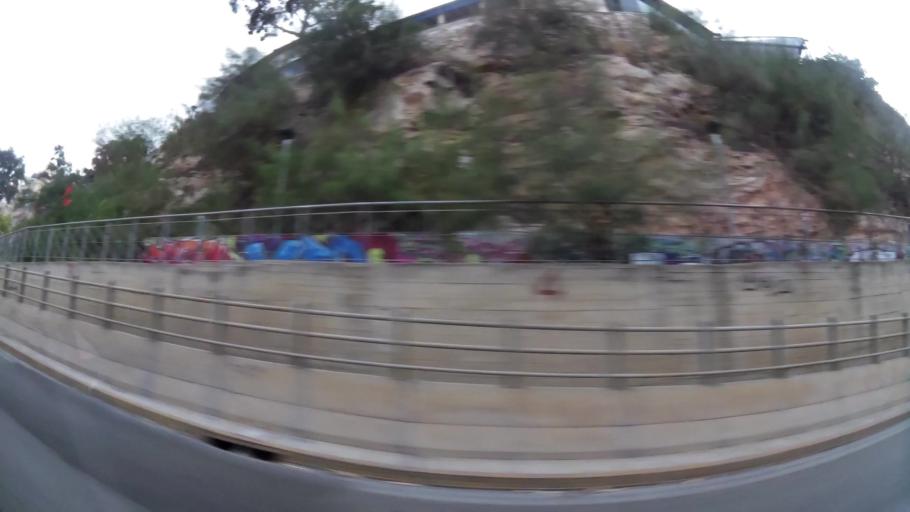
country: GR
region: Attica
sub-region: Nomos Attikis
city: Piraeus
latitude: 37.9448
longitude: 23.6299
